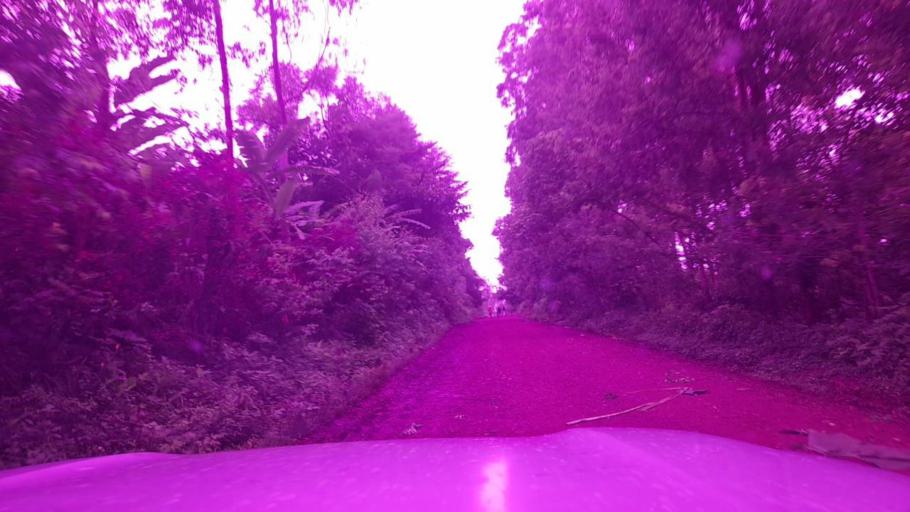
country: ET
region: Southern Nations, Nationalities, and People's Region
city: Bonga
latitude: 7.5829
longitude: 36.0194
